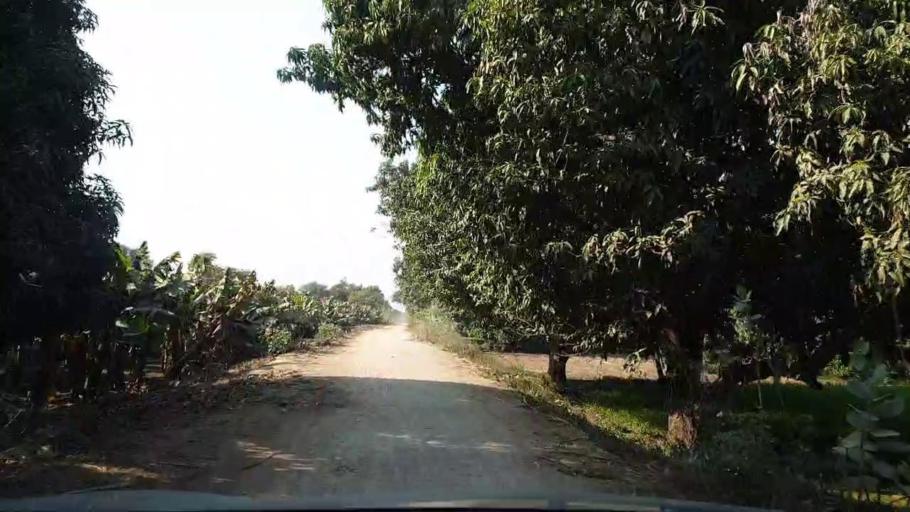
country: PK
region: Sindh
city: Tando Allahyar
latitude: 25.5474
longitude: 68.7700
